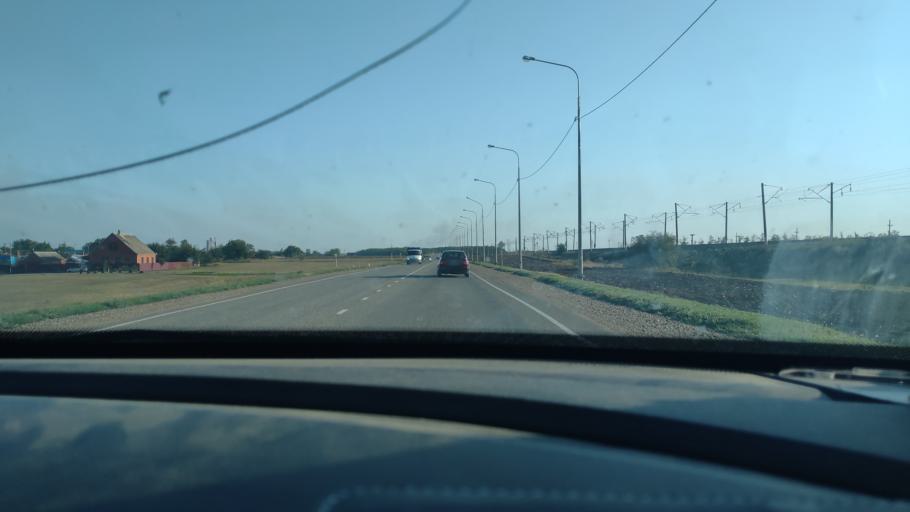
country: RU
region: Krasnodarskiy
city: Novominskaya
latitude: 46.3138
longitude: 38.9306
